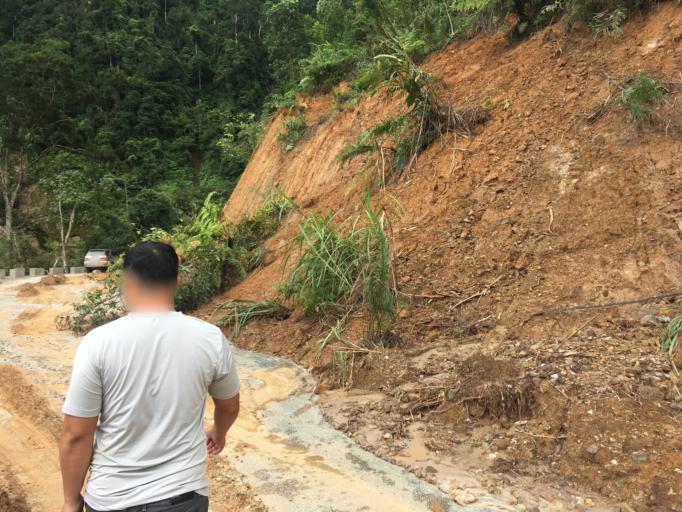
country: VN
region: Ha Giang
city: Thi Tran Tam Son
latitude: 22.9815
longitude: 105.0586
